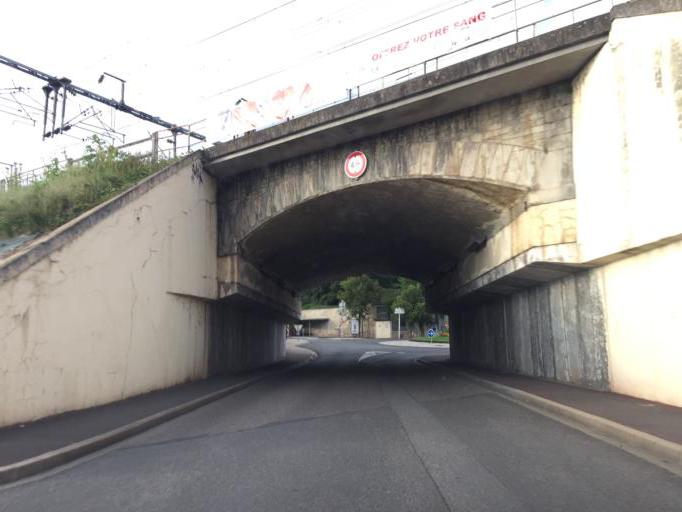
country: FR
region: Auvergne
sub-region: Departement de l'Allier
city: Saint-Germain-des-Fosses
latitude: 46.2068
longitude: 3.4332
